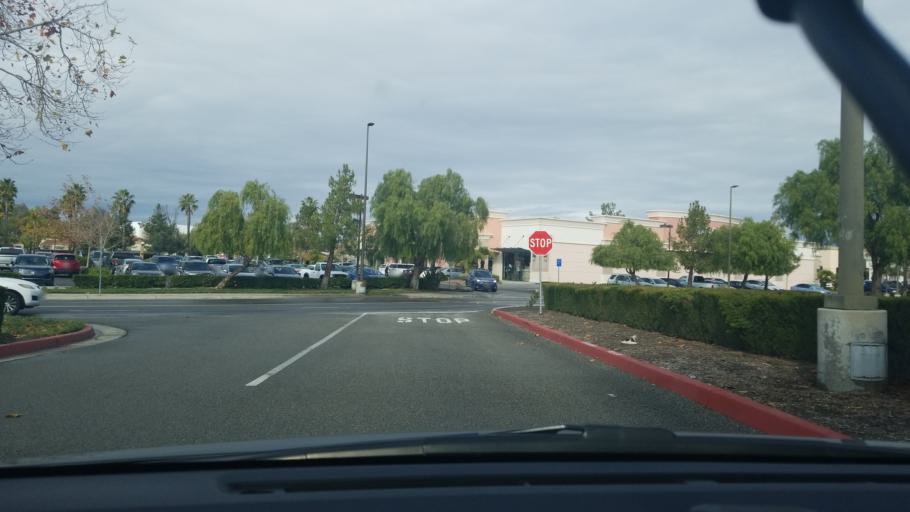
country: US
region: California
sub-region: Riverside County
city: Murrieta Hot Springs
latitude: 33.5271
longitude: -117.1550
